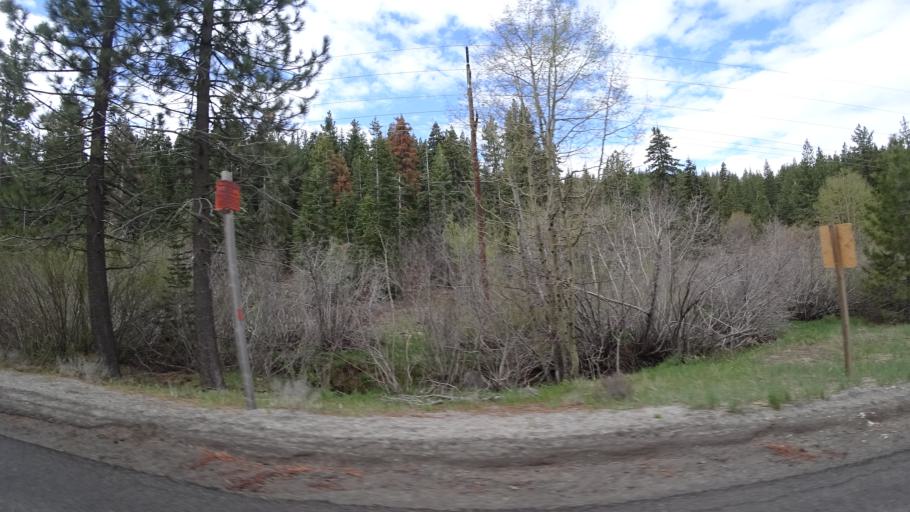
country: US
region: California
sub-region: Placer County
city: Tahoe Vista
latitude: 39.2752
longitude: -120.1016
